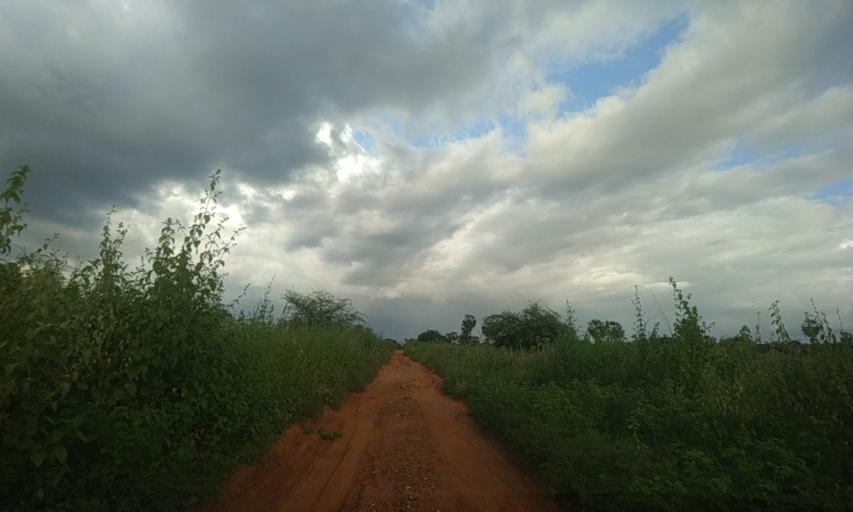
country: BR
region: Rio Grande do Norte
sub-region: Mossoro
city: Mossoro
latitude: -5.2191
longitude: -37.3462
